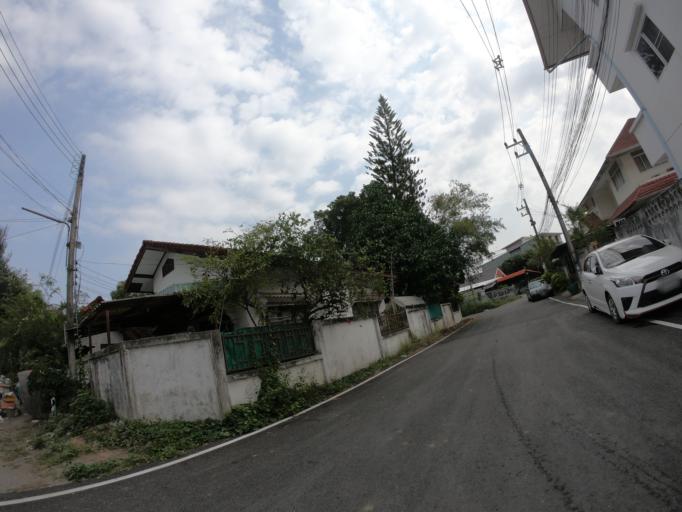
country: TH
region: Chiang Mai
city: Chiang Mai
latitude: 18.7630
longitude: 98.9706
